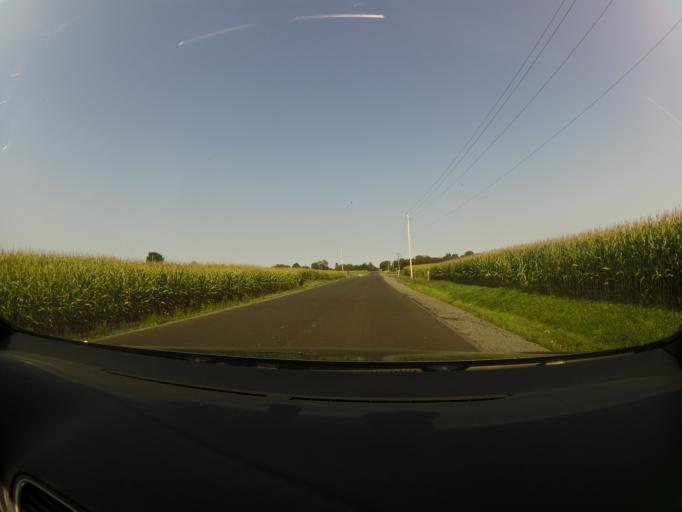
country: CA
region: Ontario
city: Carleton Place
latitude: 45.3292
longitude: -76.0894
